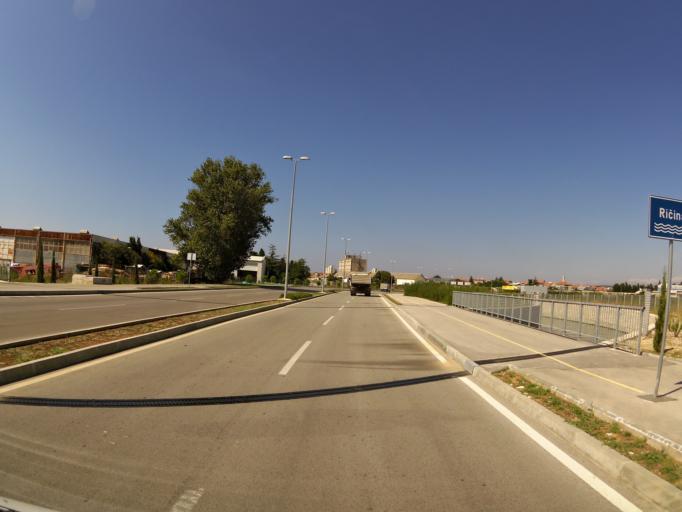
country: HR
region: Zadarska
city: Zadar
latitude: 44.0974
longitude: 15.2571
